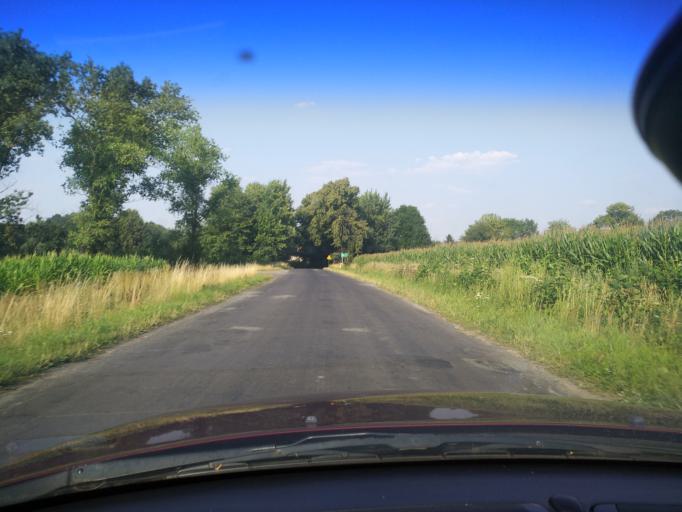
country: PL
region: Lower Silesian Voivodeship
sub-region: Powiat zgorzelecki
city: Sulikow
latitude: 51.0853
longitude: 15.1305
